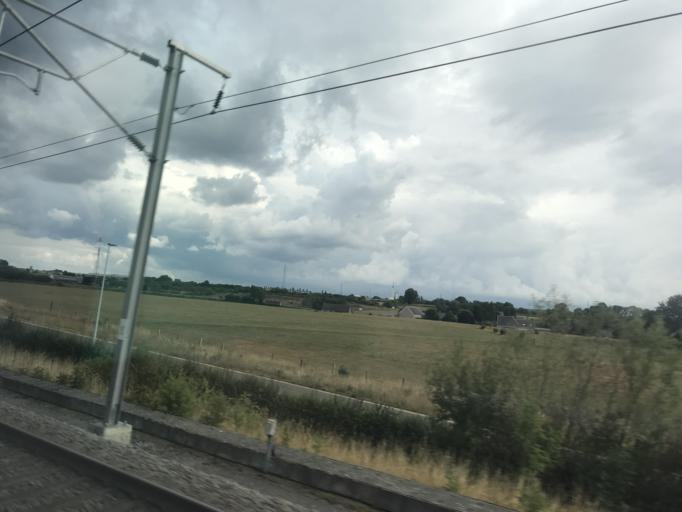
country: BE
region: Wallonia
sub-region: Province de Liege
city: Baelen
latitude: 50.6465
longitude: 5.9899
